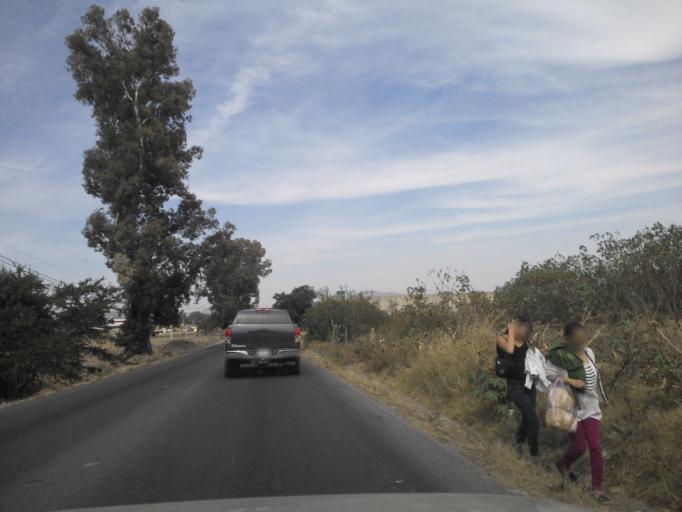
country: MX
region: Jalisco
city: San Sebastian el Grande
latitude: 20.5126
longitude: -103.4121
